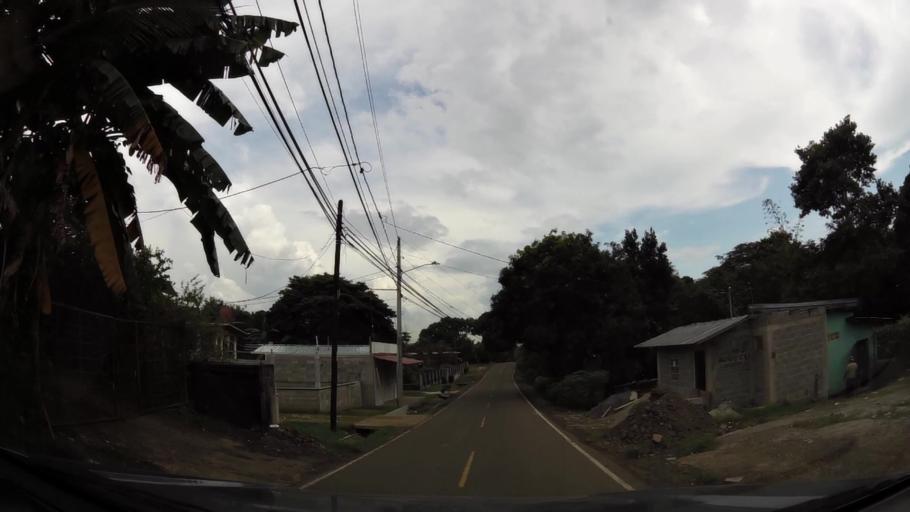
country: PA
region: Panama
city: Tocumen
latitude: 9.1138
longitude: -79.3724
